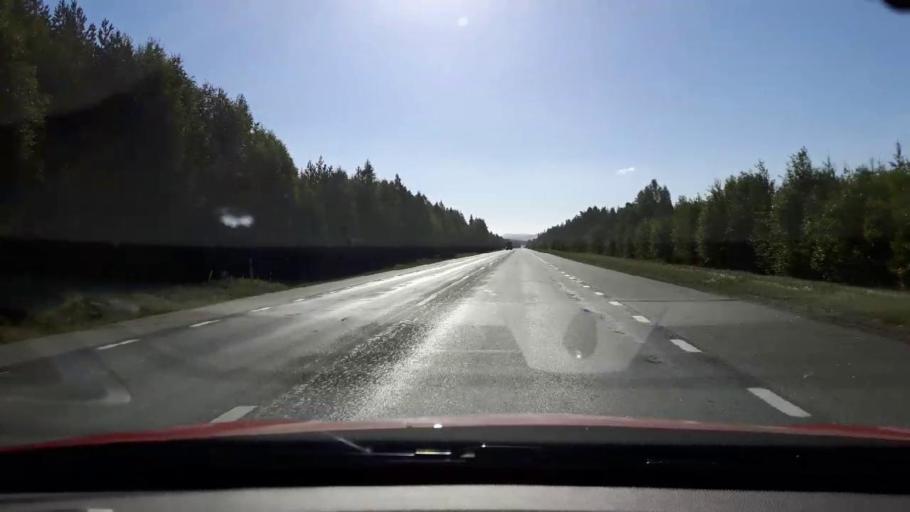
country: SE
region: Vaesternorrland
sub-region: Ange Kommun
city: Ange
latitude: 62.5937
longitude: 15.7088
